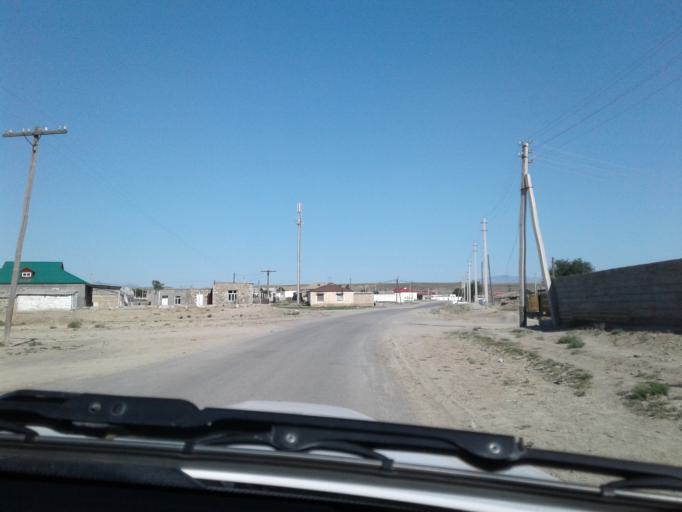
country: TM
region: Balkan
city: Serdar
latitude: 38.7137
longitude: 56.3361
